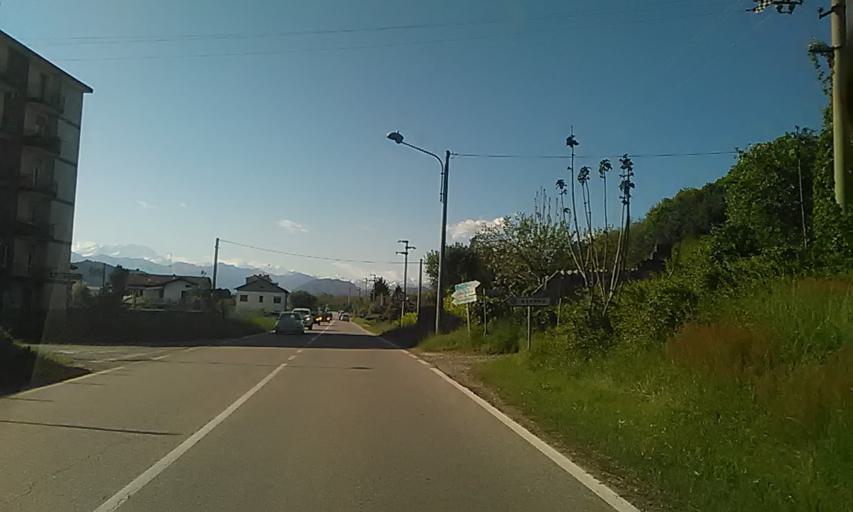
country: IT
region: Piedmont
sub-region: Provincia di Novara
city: Ghemme
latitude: 45.6008
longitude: 8.4250
